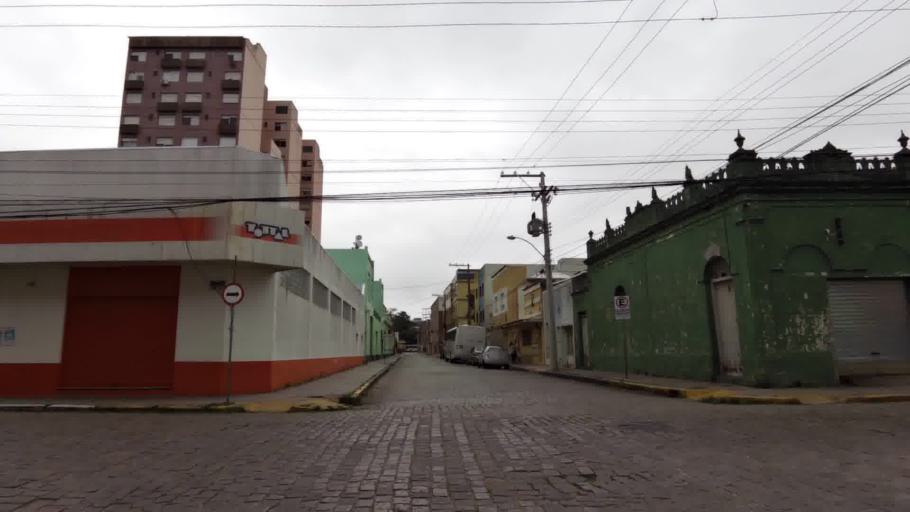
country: BR
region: Rio Grande do Sul
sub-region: Rio Grande
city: Rio Grande
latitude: -32.0299
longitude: -52.0991
